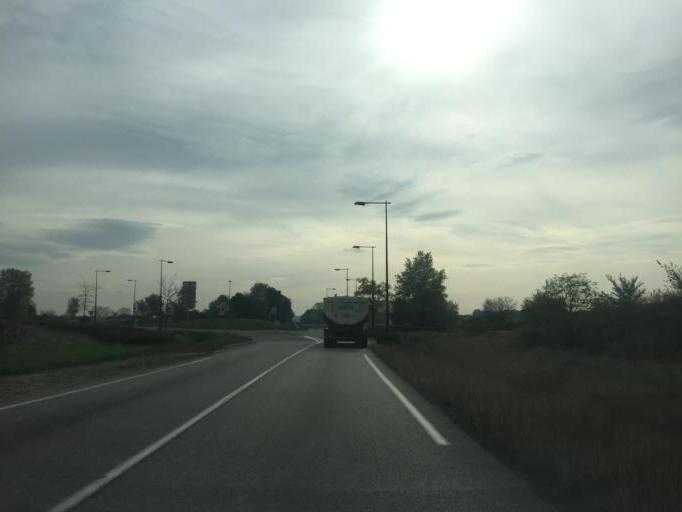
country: FR
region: Rhone-Alpes
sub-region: Departement de l'Ain
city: La Boisse
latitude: 45.8394
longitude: 5.0500
